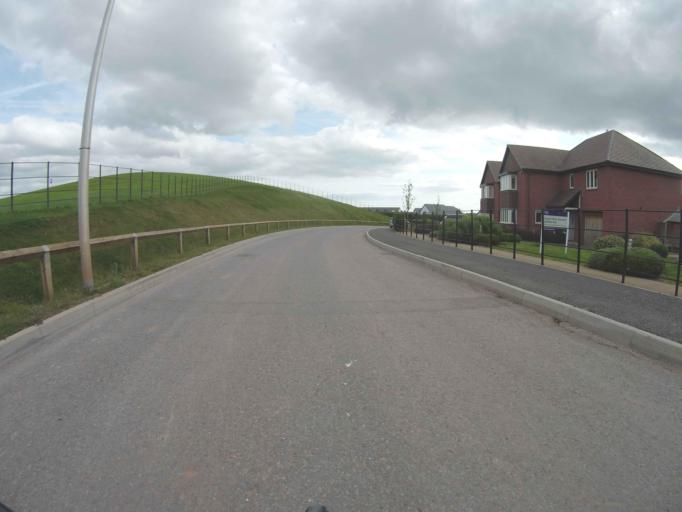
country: GB
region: England
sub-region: Devon
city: Exmouth
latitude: 50.6230
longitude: -3.3845
